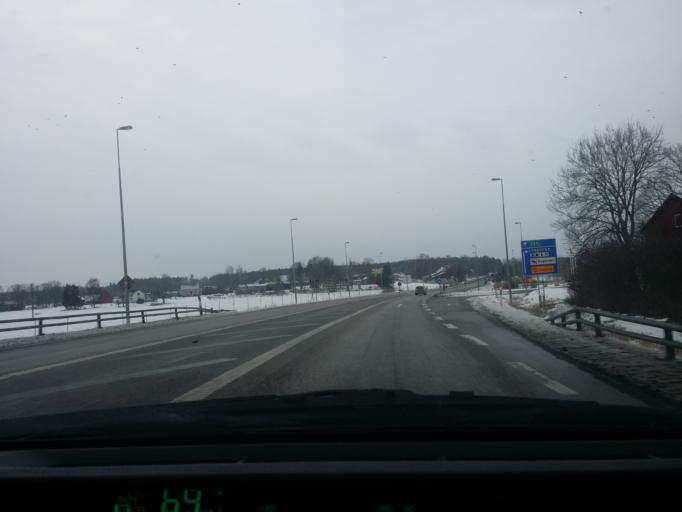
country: SE
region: Vaestra Goetaland
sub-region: Toreboda Kommun
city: Toereboda
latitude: 58.7989
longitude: 14.0571
